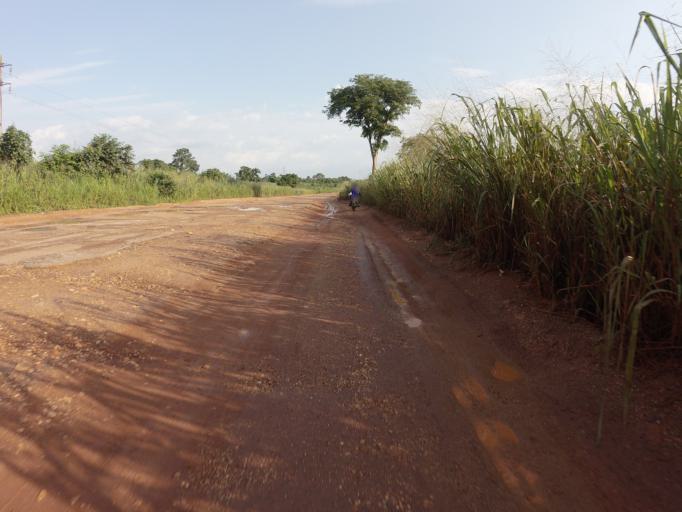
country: GH
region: Volta
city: Hohoe
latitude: 7.0877
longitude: 0.4449
